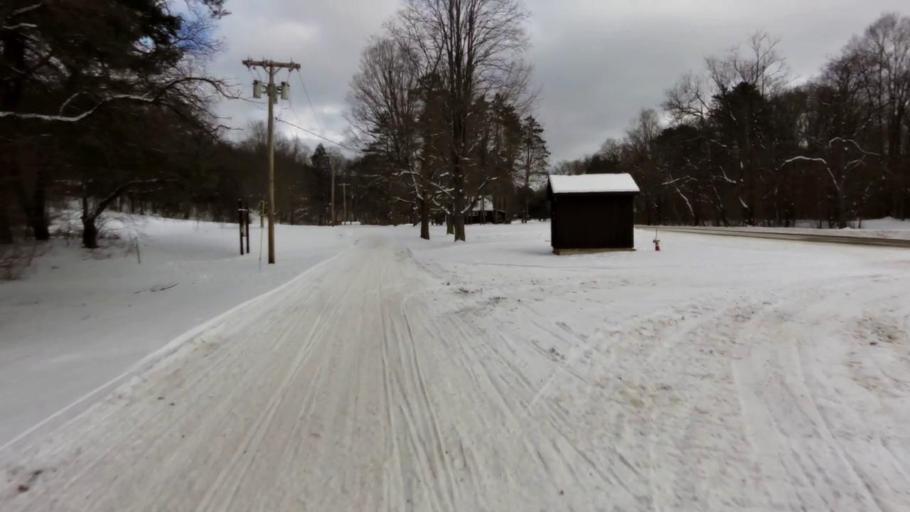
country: US
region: New York
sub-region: Cattaraugus County
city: Salamanca
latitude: 42.0110
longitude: -78.8233
